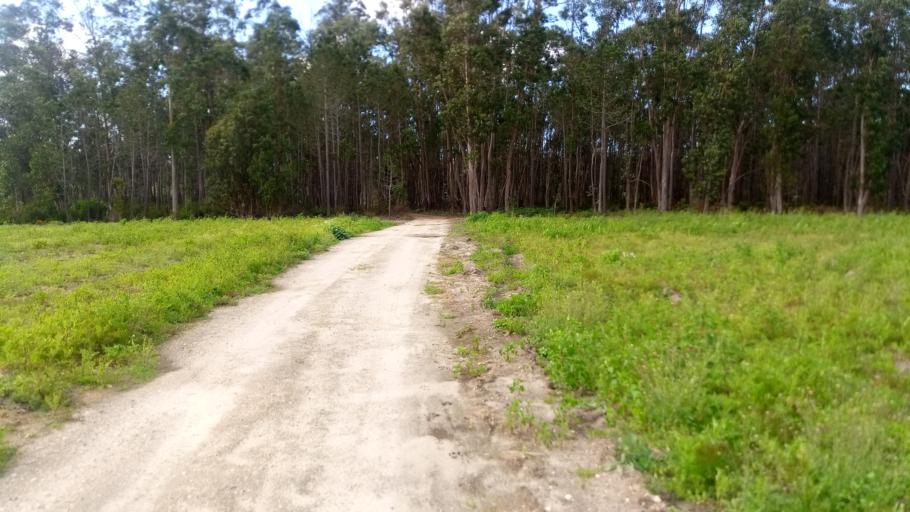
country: PT
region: Leiria
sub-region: Caldas da Rainha
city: Caldas da Rainha
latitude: 39.4355
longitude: -9.1659
